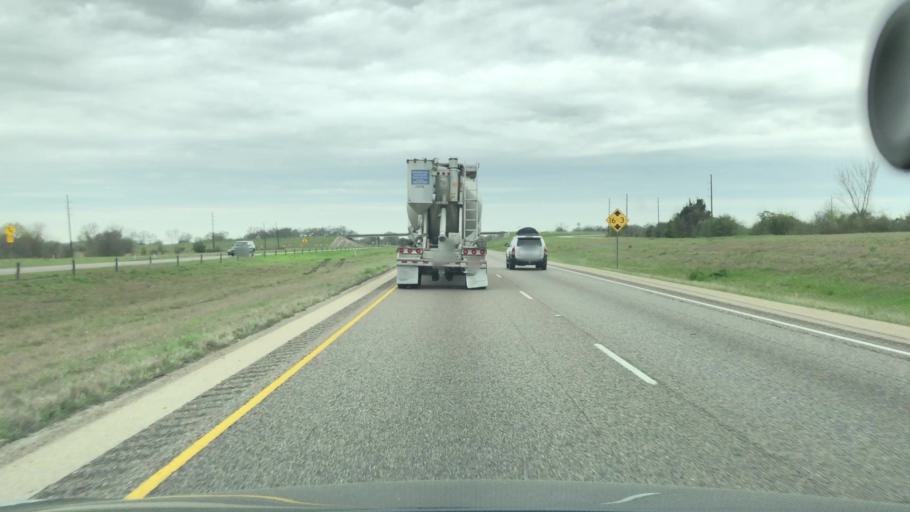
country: US
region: Texas
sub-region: Madison County
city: Madisonville
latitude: 31.0665
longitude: -95.9522
